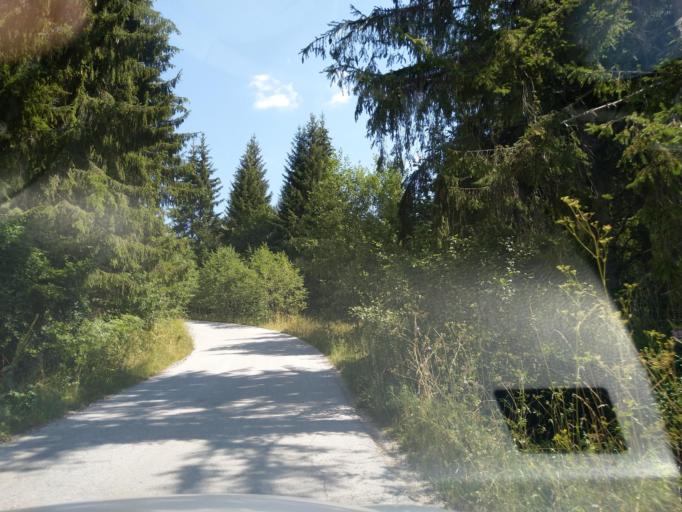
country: RS
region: Central Serbia
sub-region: Zlatiborski Okrug
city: Nova Varos
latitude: 43.4758
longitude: 19.9656
